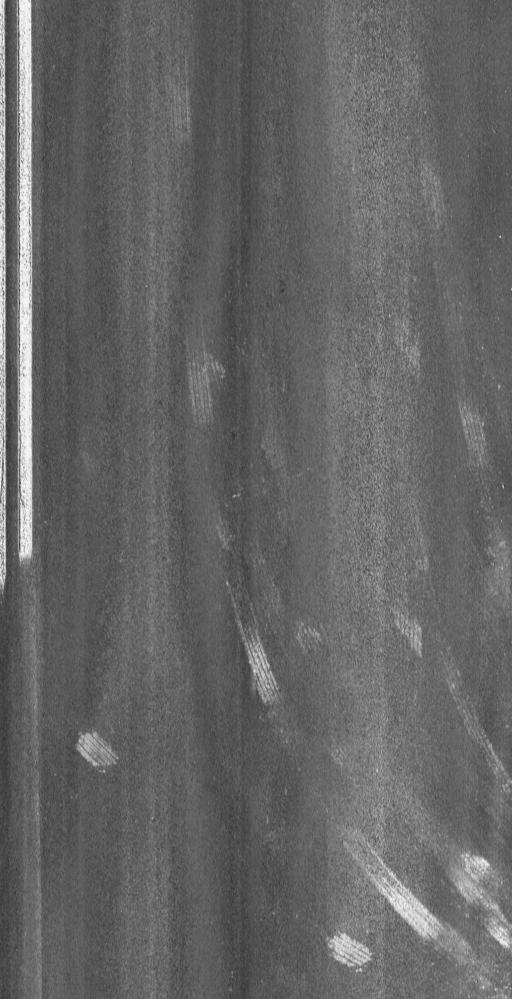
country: US
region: Vermont
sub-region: Chittenden County
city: Burlington
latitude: 44.3718
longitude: -73.2250
